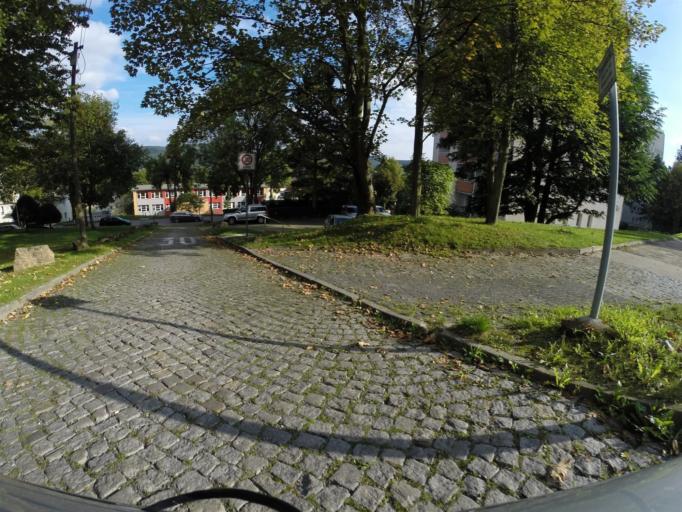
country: DE
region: Thuringia
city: Jena
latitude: 50.9512
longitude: 11.5969
